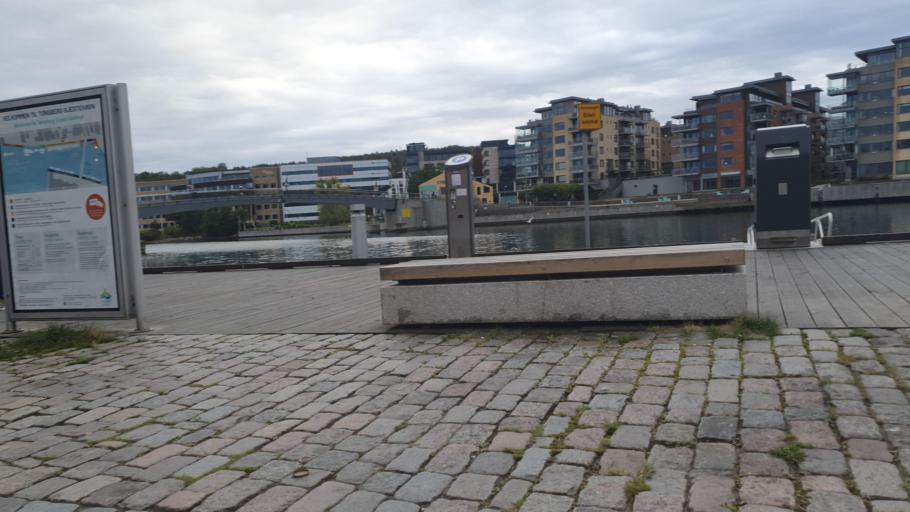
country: NO
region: Vestfold
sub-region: Tonsberg
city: Tonsberg
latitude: 59.2661
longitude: 10.4056
